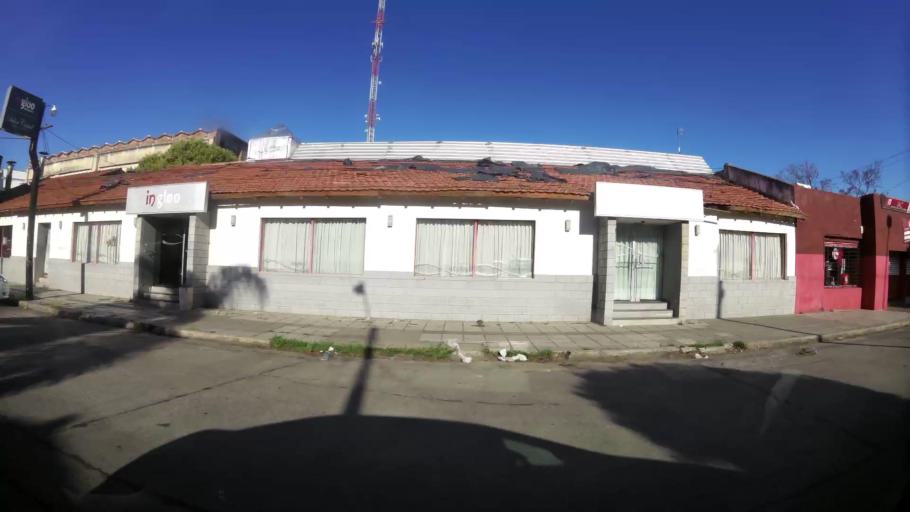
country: AR
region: Cordoba
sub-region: Departamento de Capital
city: Cordoba
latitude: -31.3849
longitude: -64.1810
